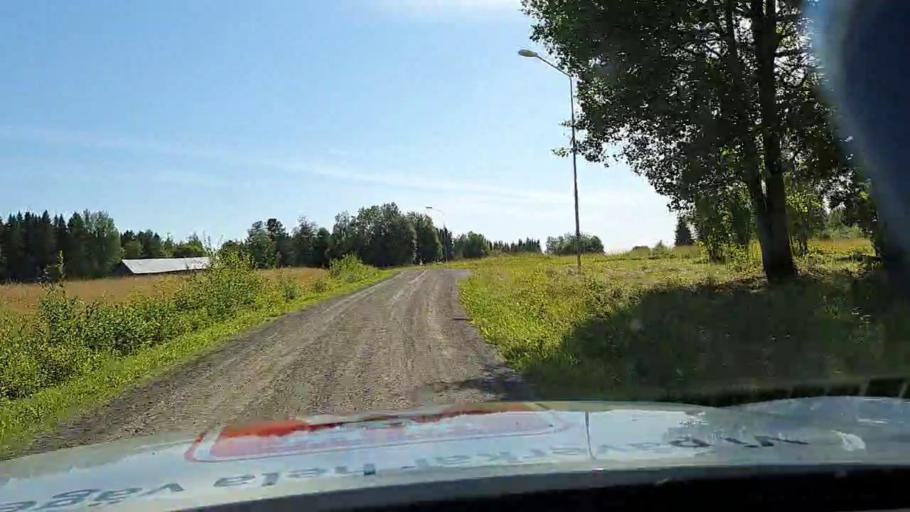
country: SE
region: Jaemtland
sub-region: Stroemsunds Kommun
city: Stroemsund
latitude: 63.7757
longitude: 15.3200
